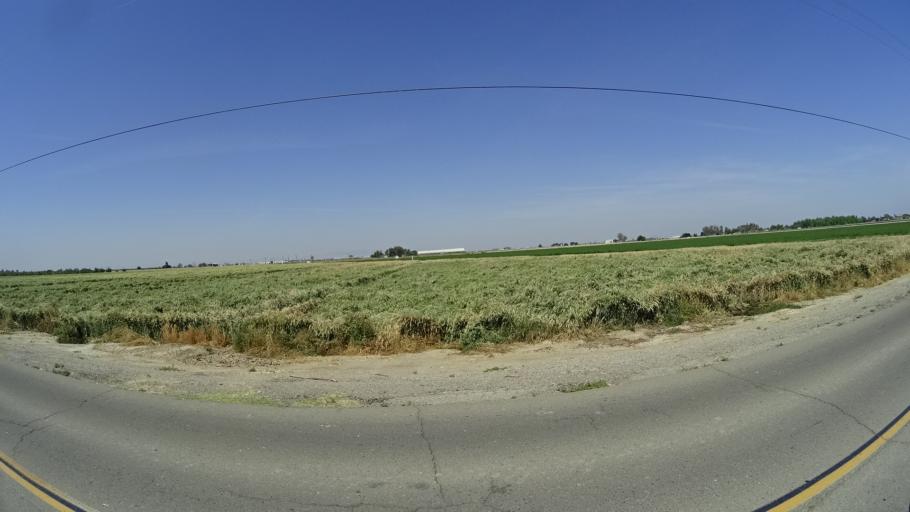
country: US
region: California
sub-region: Fresno County
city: Riverdale
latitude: 36.4160
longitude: -119.8513
